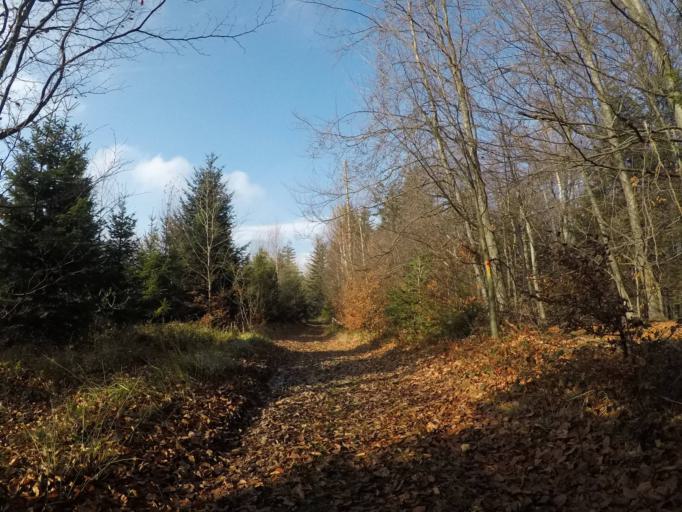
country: SK
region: Kosicky
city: Gelnica
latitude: 48.7642
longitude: 21.0662
